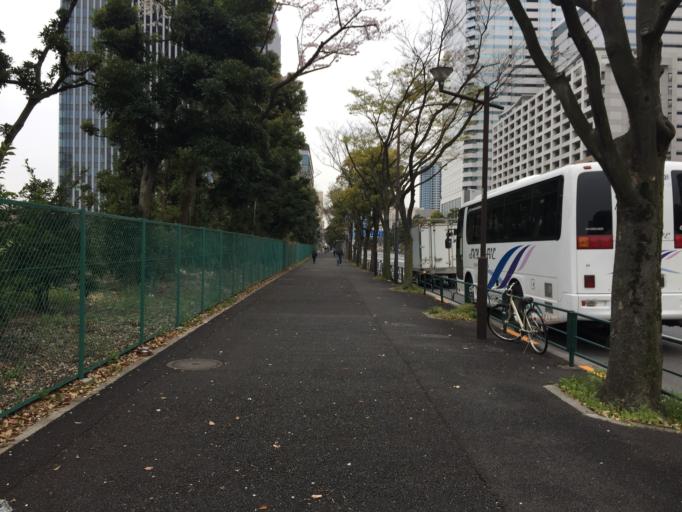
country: JP
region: Tokyo
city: Tokyo
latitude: 35.6574
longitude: 139.7853
